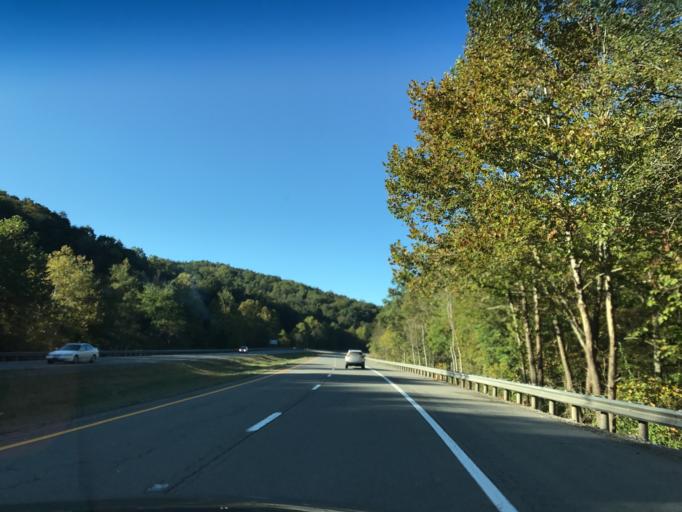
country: US
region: Ohio
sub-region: Washington County
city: Newport
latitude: 39.2574
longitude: -81.2943
